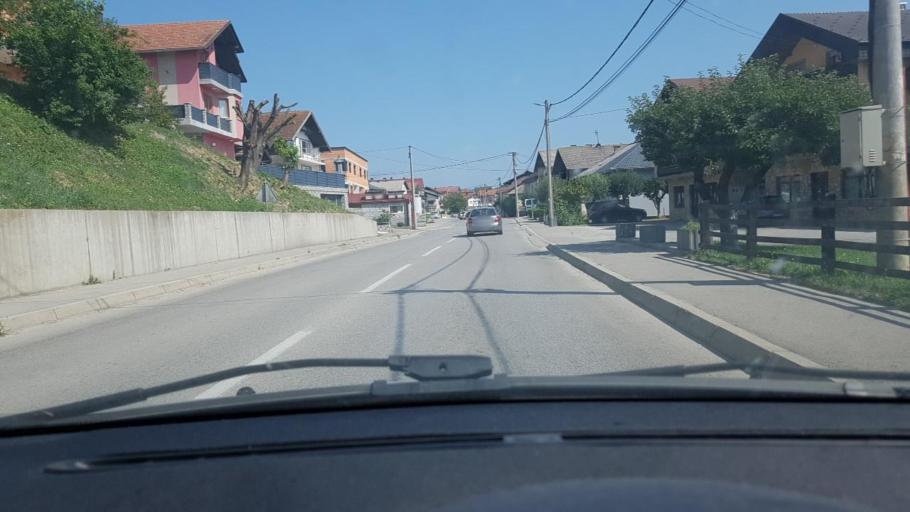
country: BA
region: Federation of Bosnia and Herzegovina
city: Velika Kladusa
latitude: 45.1876
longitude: 15.8114
